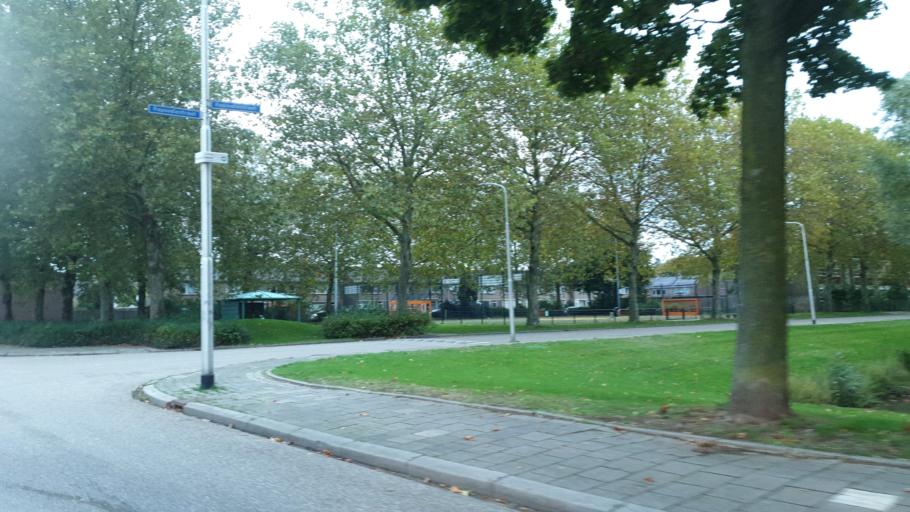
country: NL
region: Gelderland
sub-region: Gemeente Nijmegen
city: Lindenholt
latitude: 51.8320
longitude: 5.8114
